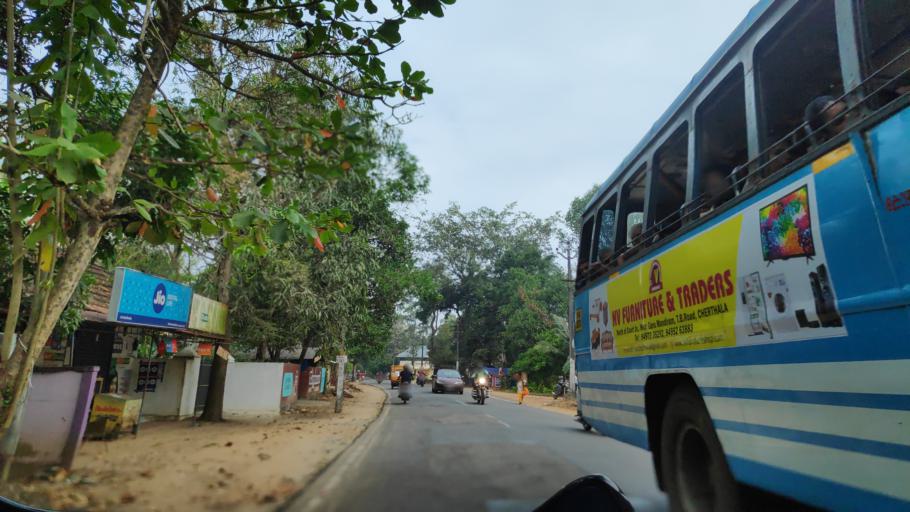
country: IN
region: Kerala
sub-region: Alappuzha
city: Vayalar
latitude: 9.7194
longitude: 76.3603
